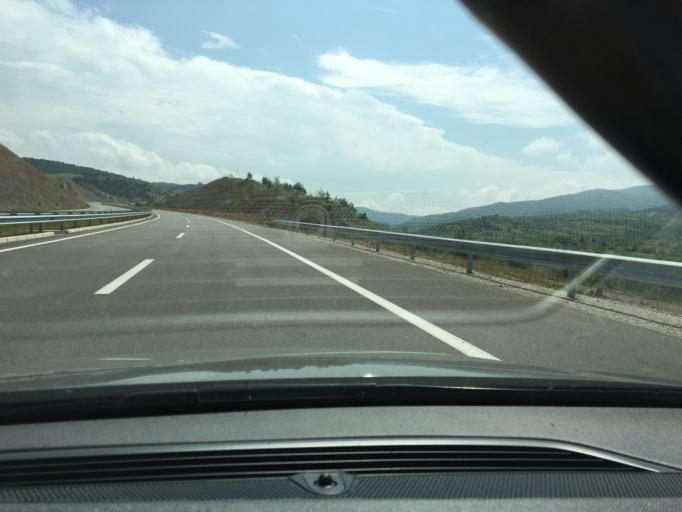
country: MK
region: Petrovec
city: Sredno Konjare
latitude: 41.9551
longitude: 21.7381
